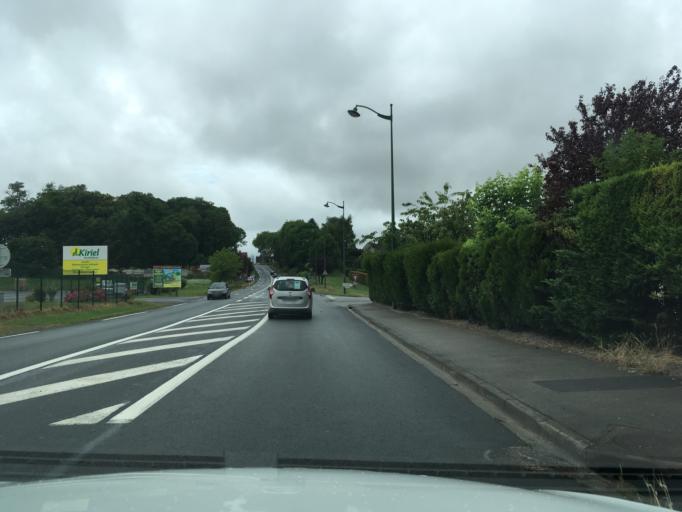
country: FR
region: Picardie
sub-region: Departement de l'Aisne
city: Homblieres
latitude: 49.8465
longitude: 3.3618
